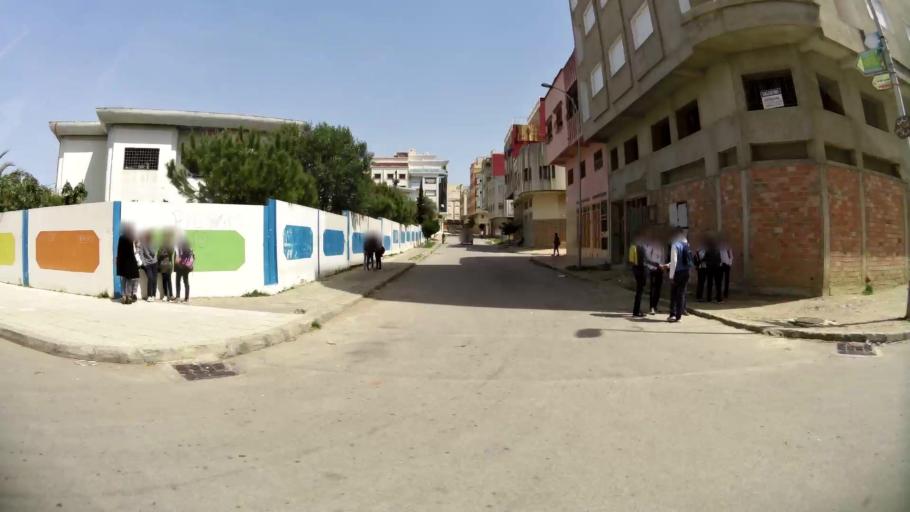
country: MA
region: Tanger-Tetouan
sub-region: Tanger-Assilah
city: Tangier
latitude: 35.7577
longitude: -5.8407
